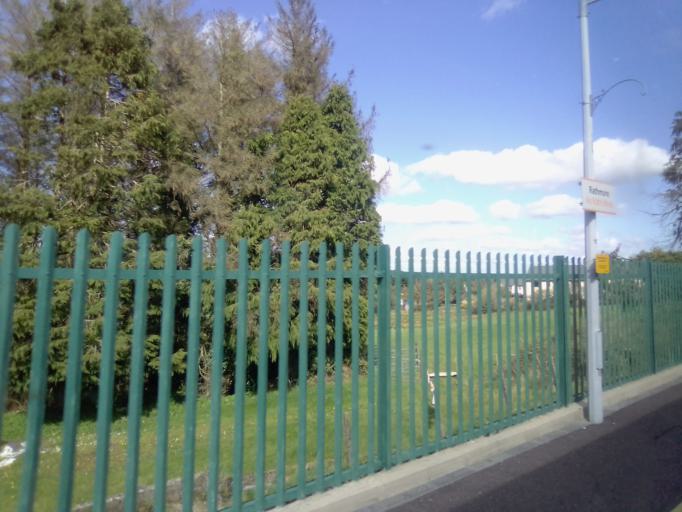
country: IE
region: Munster
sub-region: County Cork
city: Millstreet
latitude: 52.0854
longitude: -9.2180
